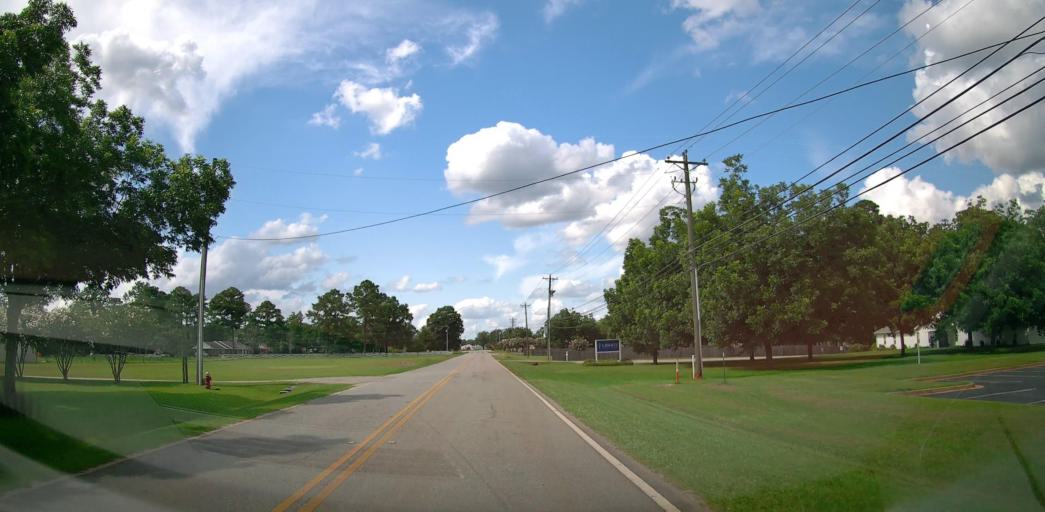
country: US
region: Georgia
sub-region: Houston County
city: Centerville
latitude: 32.5854
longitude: -83.6664
